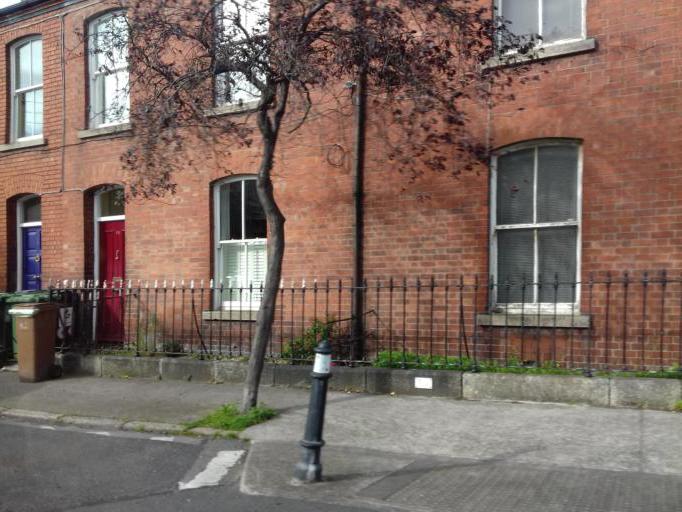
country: IE
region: Leinster
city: Rialto
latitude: 53.3344
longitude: -6.2812
